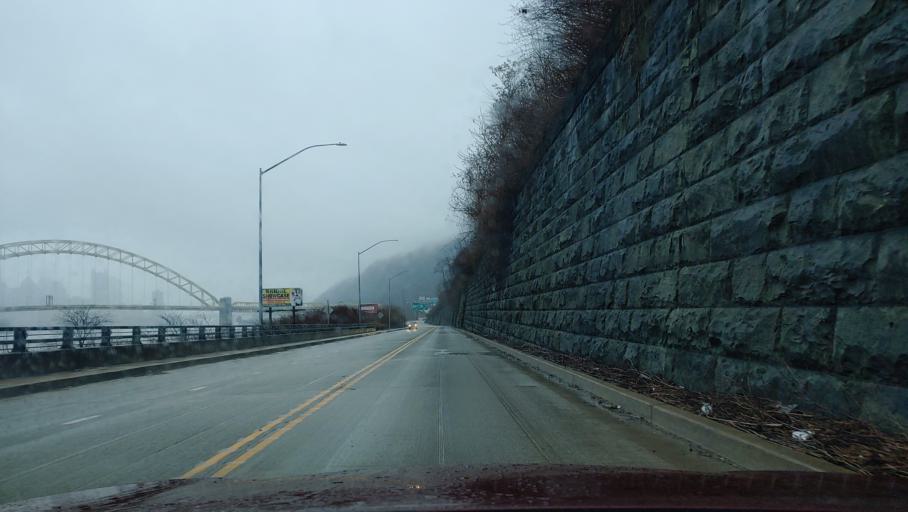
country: US
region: Pennsylvania
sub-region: Allegheny County
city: Ingram
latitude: 40.4481
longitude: -80.0335
